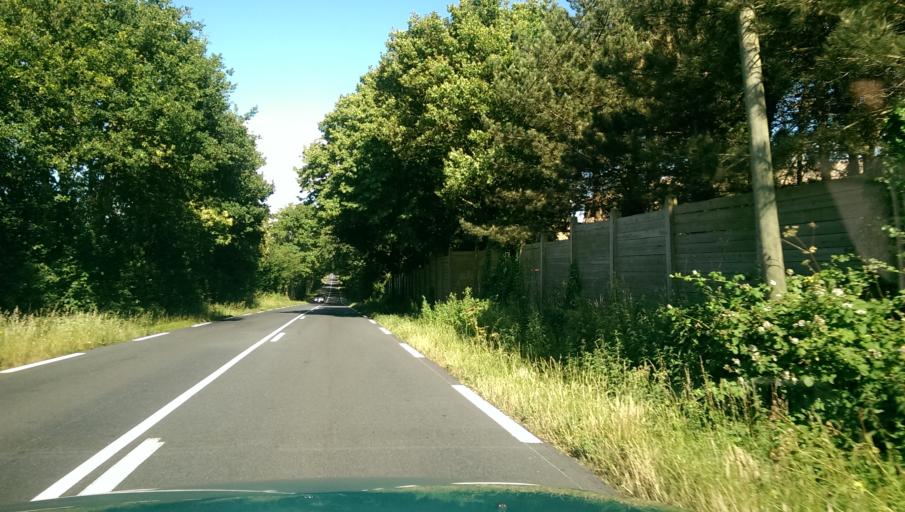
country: FR
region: Pays de la Loire
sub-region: Departement de la Vendee
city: Falleron
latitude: 46.8824
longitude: -1.6848
